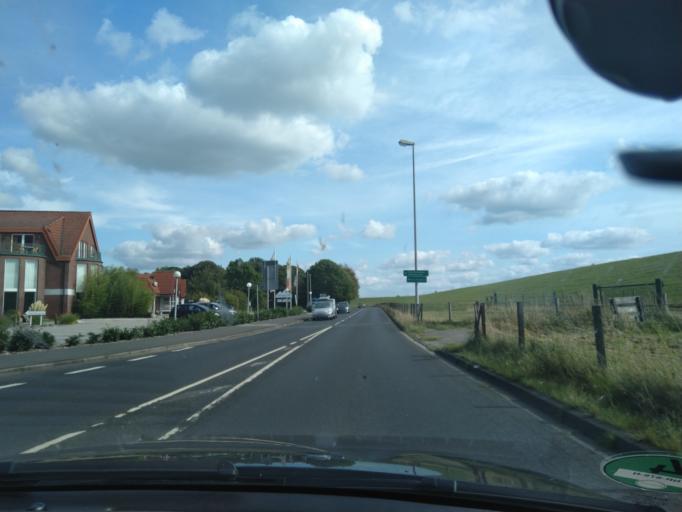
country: DE
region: Lower Saxony
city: Leer
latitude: 53.2154
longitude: 7.4394
